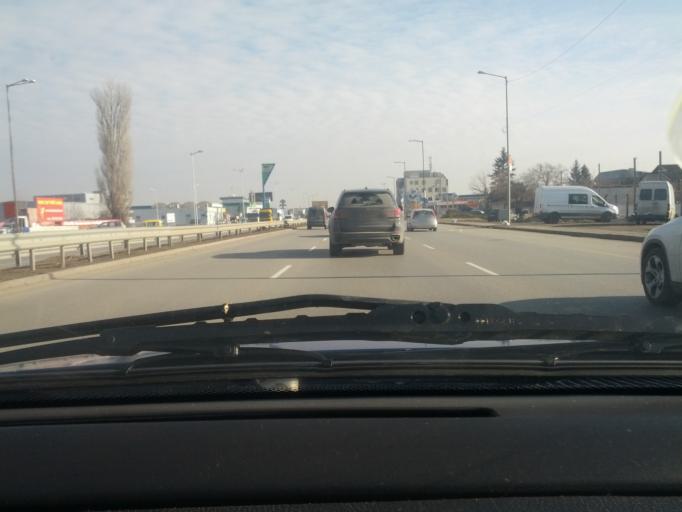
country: BG
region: Sofia-Capital
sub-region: Stolichna Obshtina
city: Sofia
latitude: 42.7093
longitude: 23.4261
